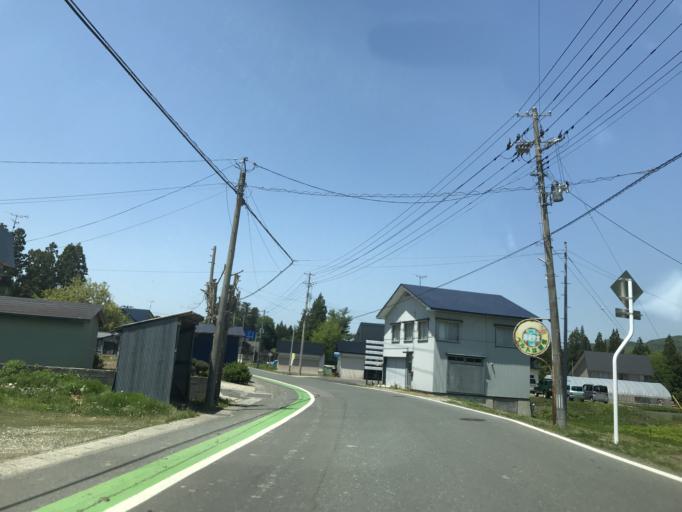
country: JP
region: Akita
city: Yokotemachi
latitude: 39.3521
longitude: 140.7694
